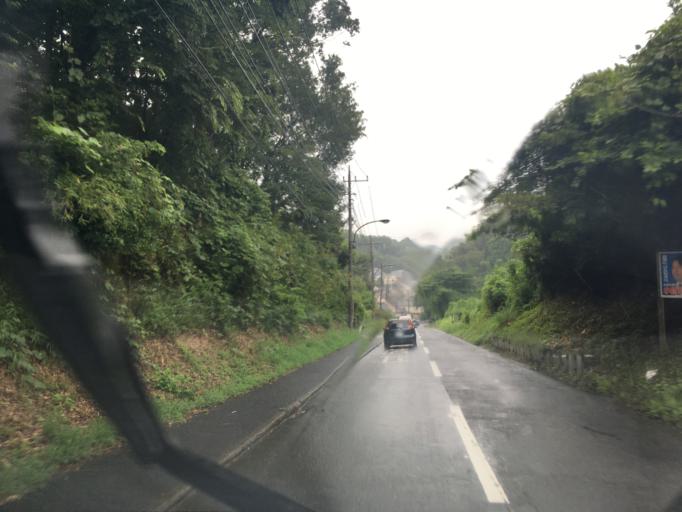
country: JP
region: Tokyo
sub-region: Machida-shi
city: Machida
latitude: 35.6052
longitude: 139.4282
